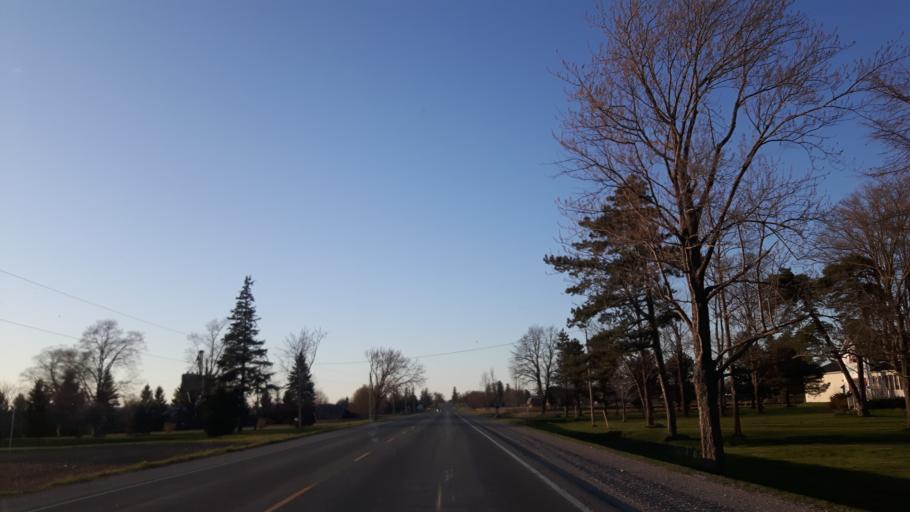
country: CA
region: Ontario
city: Bluewater
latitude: 43.5750
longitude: -81.5276
